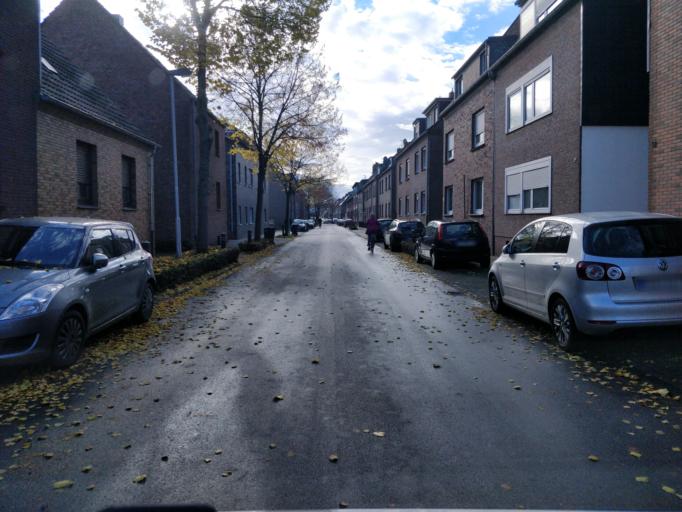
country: DE
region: North Rhine-Westphalia
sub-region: Regierungsbezirk Dusseldorf
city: Emmerich
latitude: 51.8400
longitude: 6.2474
